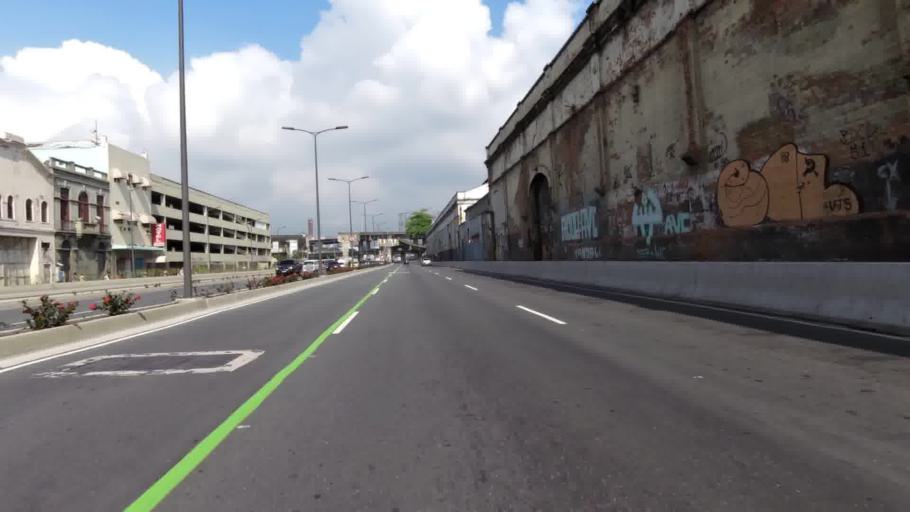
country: BR
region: Rio de Janeiro
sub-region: Rio De Janeiro
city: Rio de Janeiro
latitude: -22.8975
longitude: -43.2077
